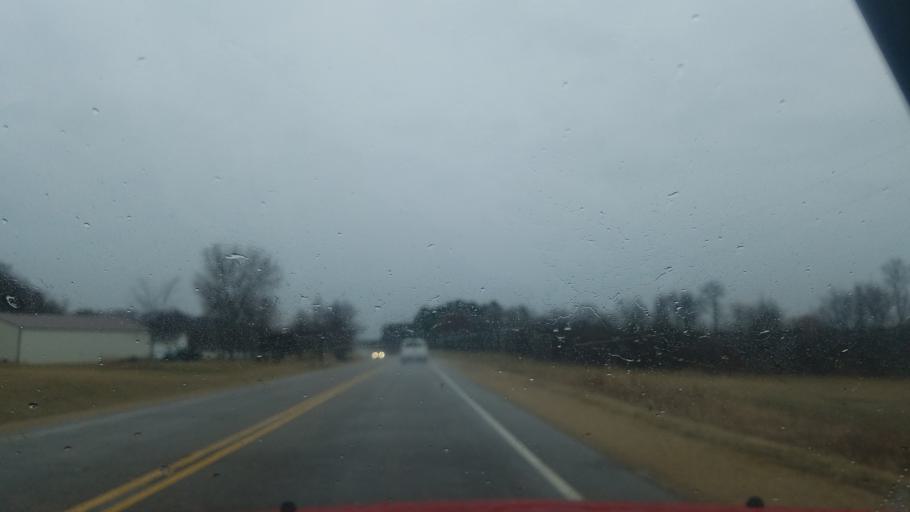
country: US
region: Wisconsin
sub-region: Dunn County
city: Tainter Lake
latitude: 45.0205
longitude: -91.8910
